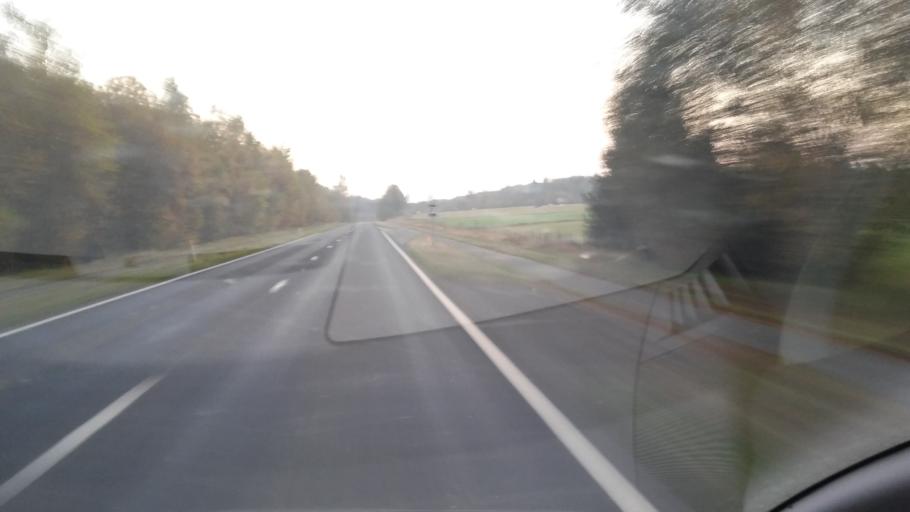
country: BE
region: Wallonia
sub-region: Province du Luxembourg
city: Etalle
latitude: 49.6472
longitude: 5.5770
